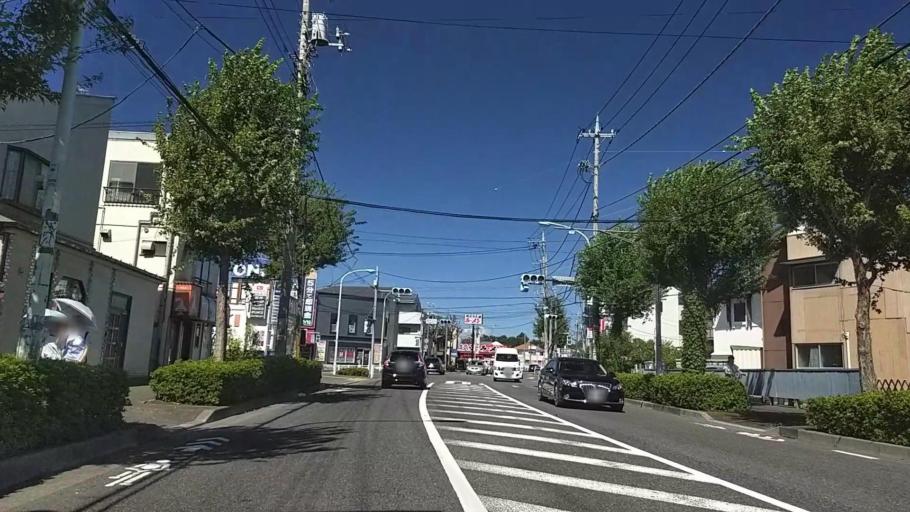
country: JP
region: Tokyo
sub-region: Machida-shi
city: Machida
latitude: 35.5843
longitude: 139.4732
